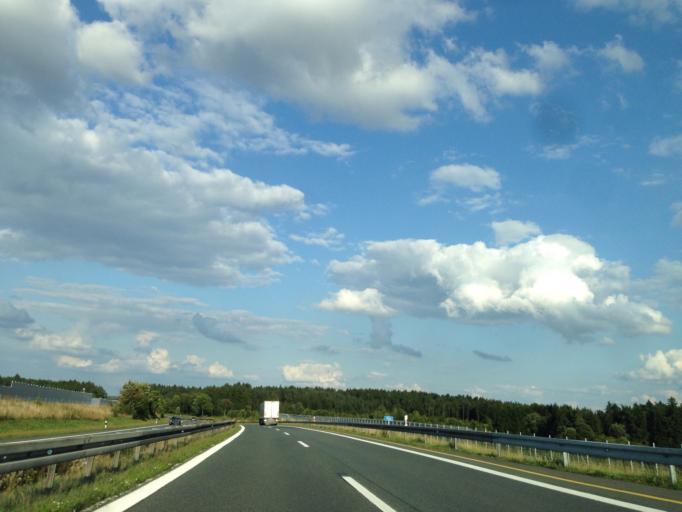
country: DE
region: Bavaria
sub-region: Upper Franconia
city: Wonsees
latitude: 50.0056
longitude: 11.2607
